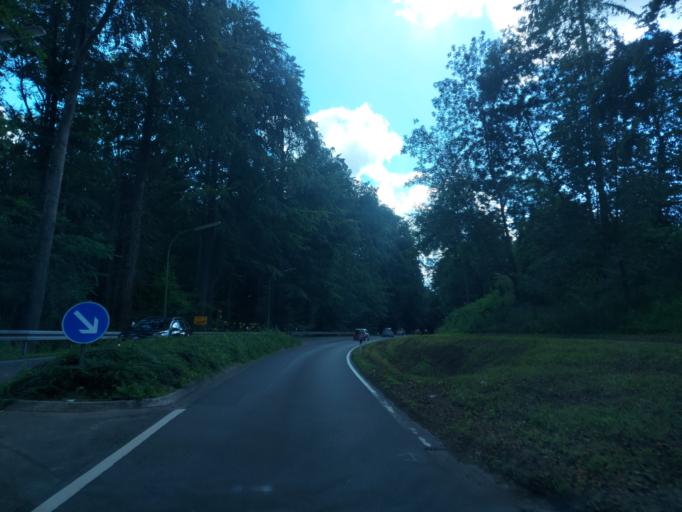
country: DE
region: Lower Saxony
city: Hagen
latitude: 52.2151
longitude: 8.0029
